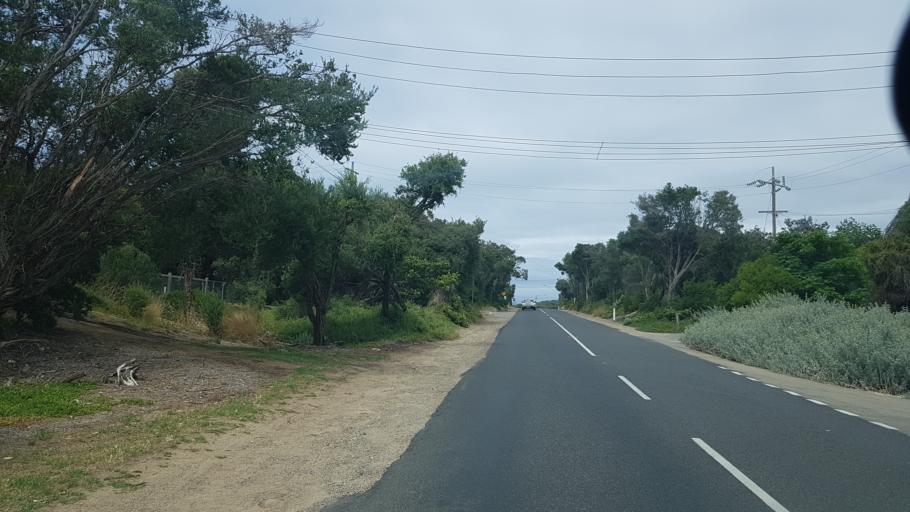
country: AU
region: Victoria
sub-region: Mornington Peninsula
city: Blairgowrie
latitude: -38.3669
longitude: 144.7734
